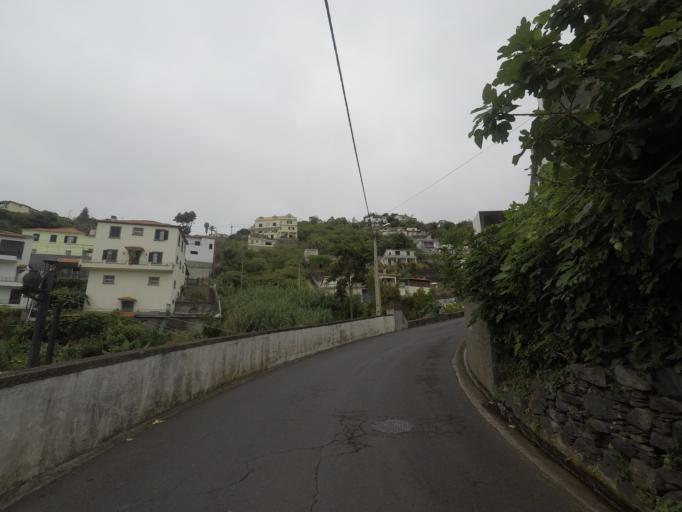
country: PT
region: Madeira
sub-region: Funchal
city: Nossa Senhora do Monte
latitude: 32.6753
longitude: -16.9412
